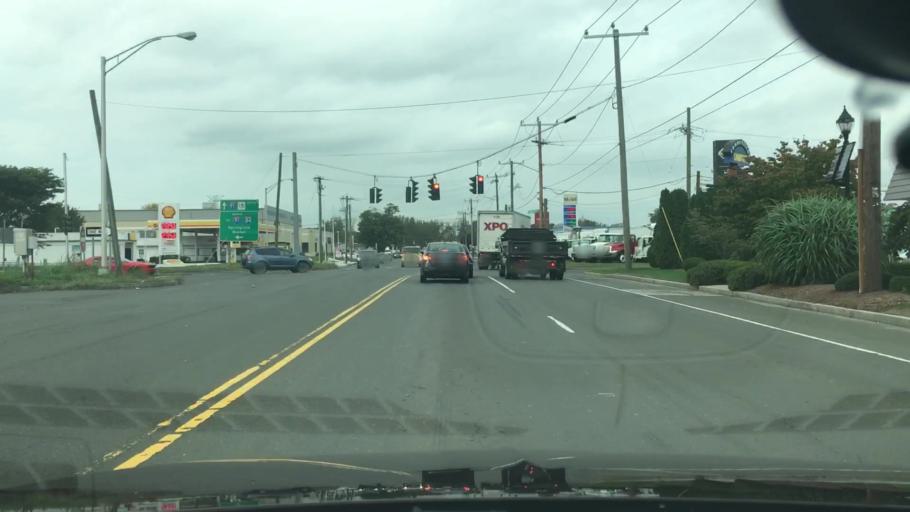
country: US
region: Connecticut
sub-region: Hartford County
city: Wethersfield
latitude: 41.7357
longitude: -72.6596
